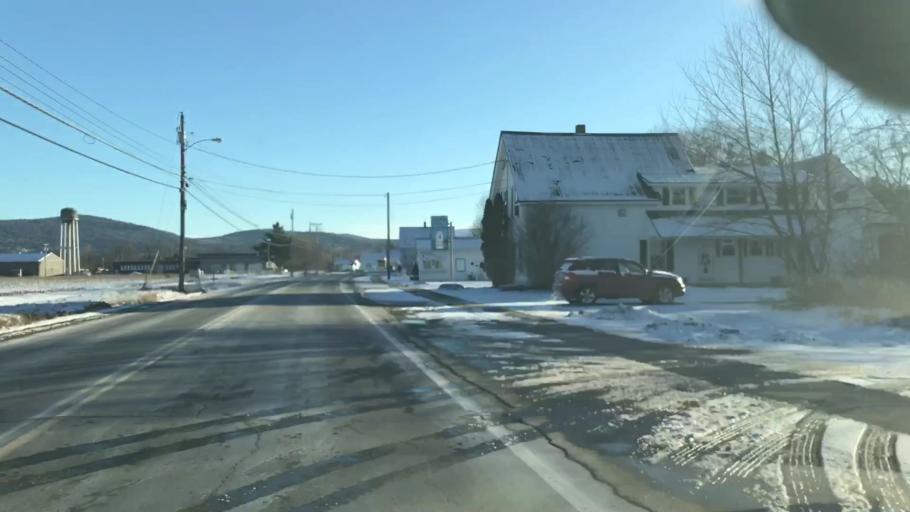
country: US
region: New Hampshire
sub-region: Grafton County
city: North Haverhill
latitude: 44.0997
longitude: -72.0258
